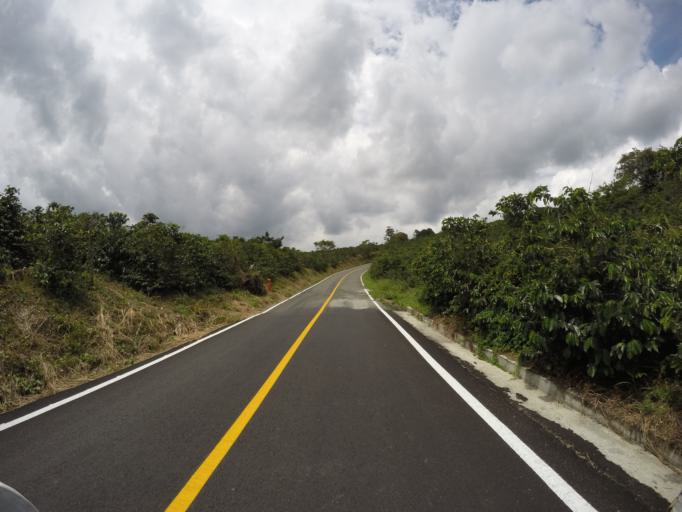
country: CO
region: Quindio
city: Quimbaya
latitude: 4.6126
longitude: -75.7445
